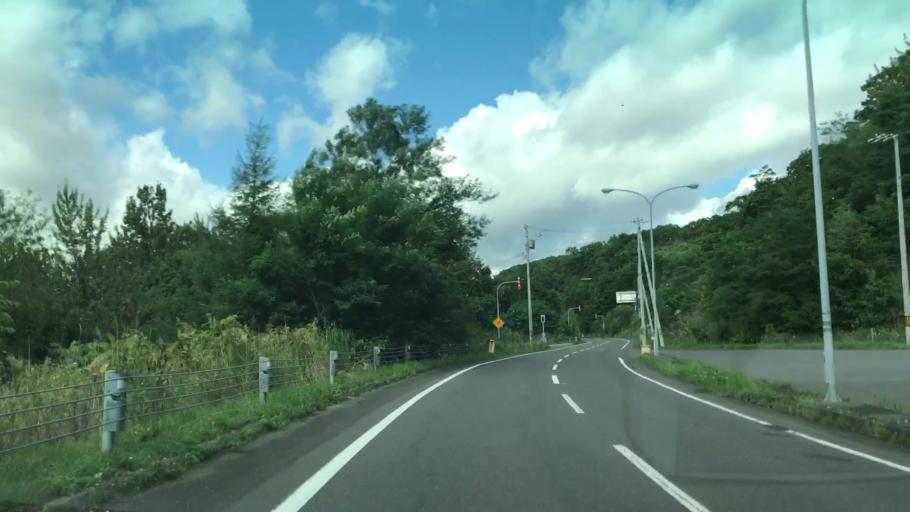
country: JP
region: Hokkaido
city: Muroran
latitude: 42.3683
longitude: 140.9555
